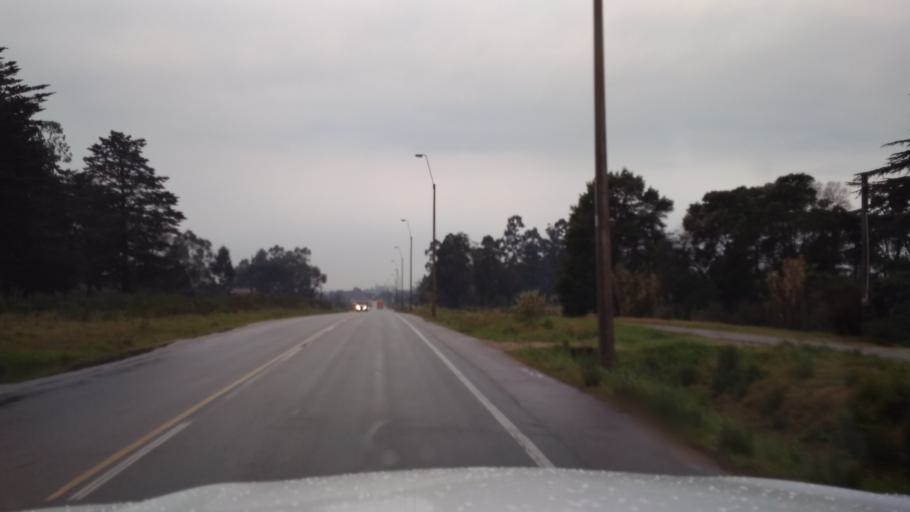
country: UY
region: Canelones
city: Toledo
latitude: -34.7613
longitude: -56.1161
